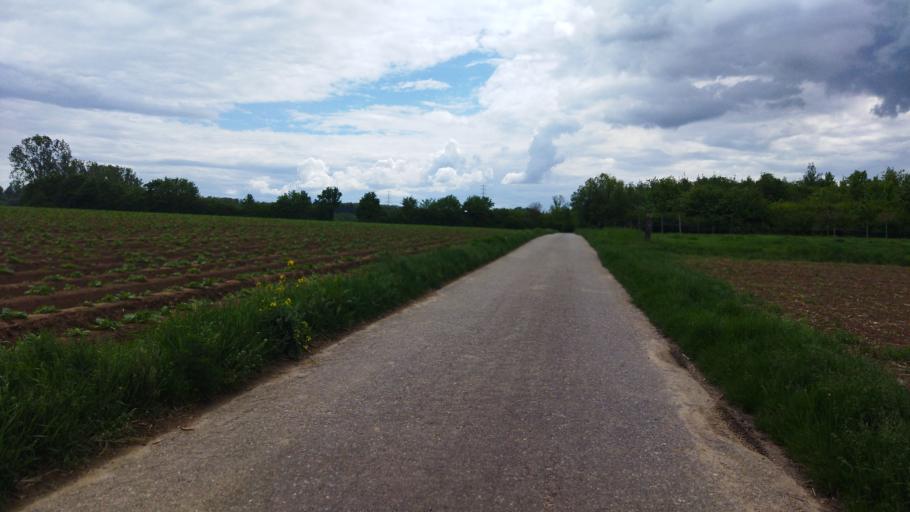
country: DE
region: Baden-Wuerttemberg
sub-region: Regierungsbezirk Stuttgart
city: Neckarwestheim
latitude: 49.0456
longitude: 9.1795
